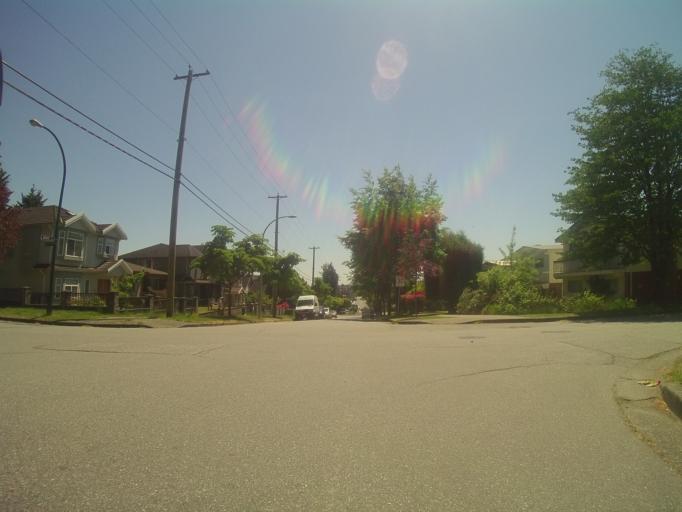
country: CA
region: British Columbia
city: Vancouver
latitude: 49.2142
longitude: -123.1066
